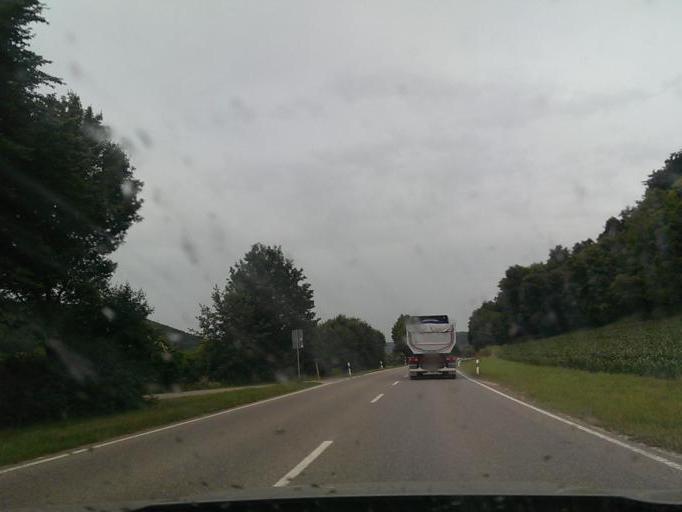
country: DE
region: Bavaria
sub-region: Upper Bavaria
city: Denkendorf
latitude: 48.9955
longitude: 11.4227
